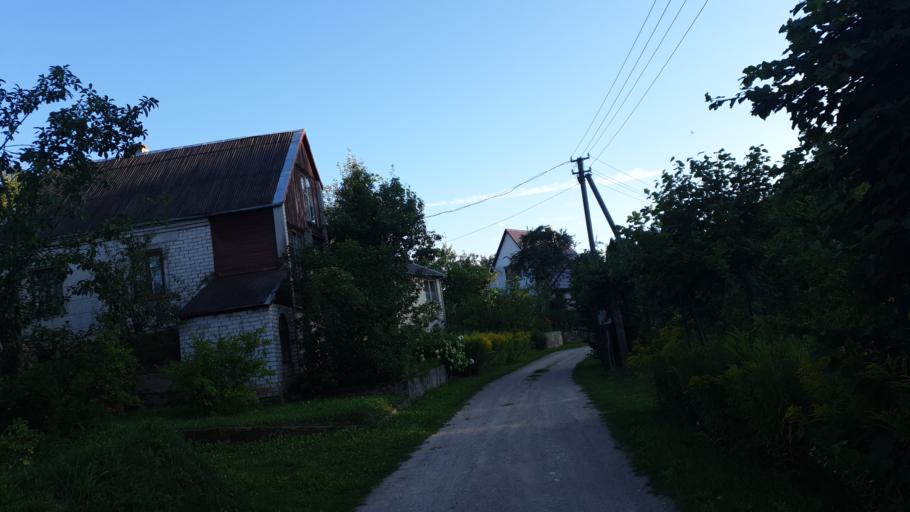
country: LT
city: Grigiskes
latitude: 54.7648
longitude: 25.0198
